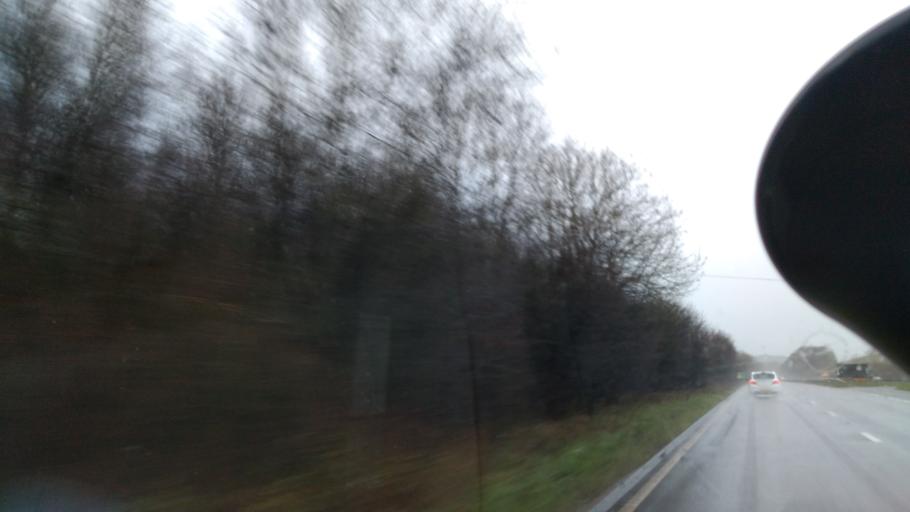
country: GB
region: England
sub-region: East Sussex
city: Lewes
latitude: 50.8663
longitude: -0.0282
